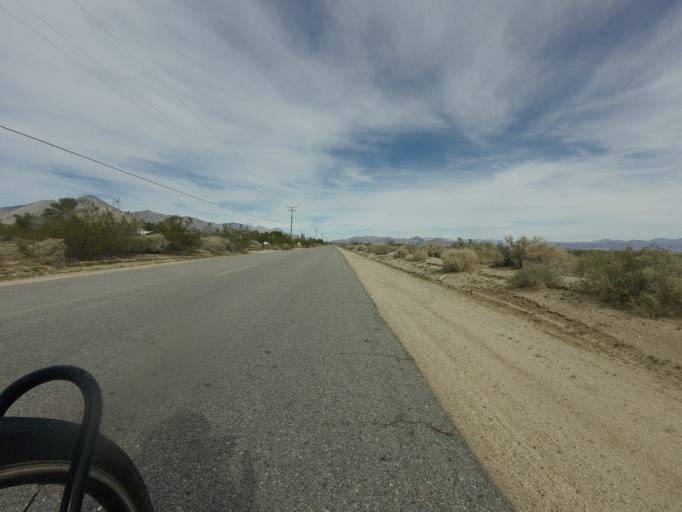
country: US
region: California
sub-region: Kern County
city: Inyokern
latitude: 35.7490
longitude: -117.8426
